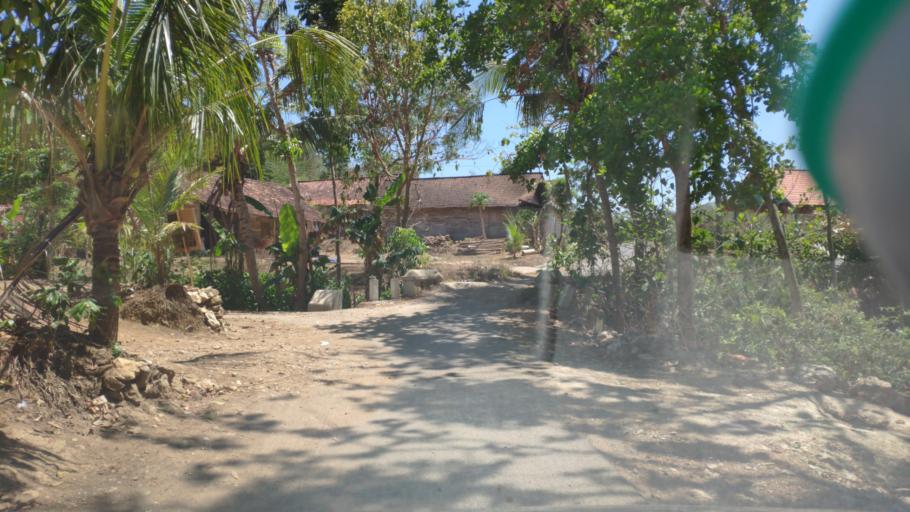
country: ID
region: Central Java
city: Blimbing
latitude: -6.9115
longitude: 111.5363
